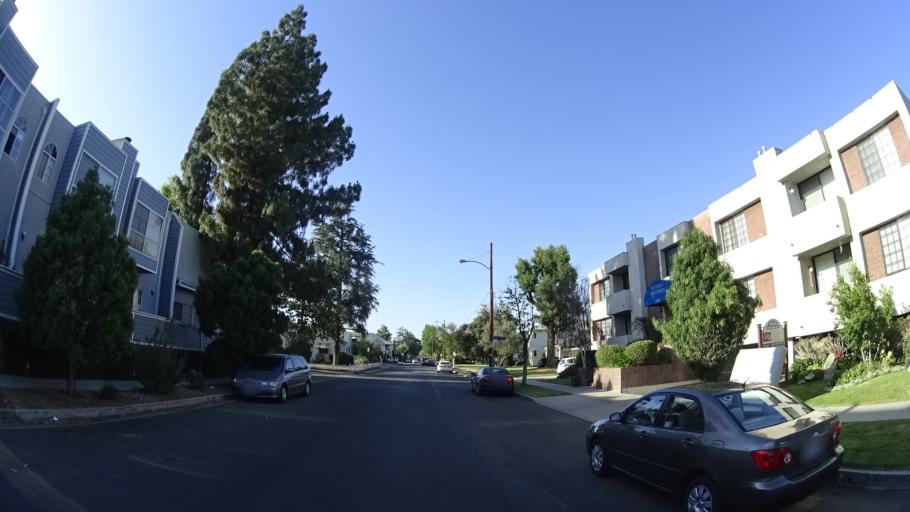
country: US
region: California
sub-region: Los Angeles County
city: North Hollywood
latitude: 34.1587
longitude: -118.3660
